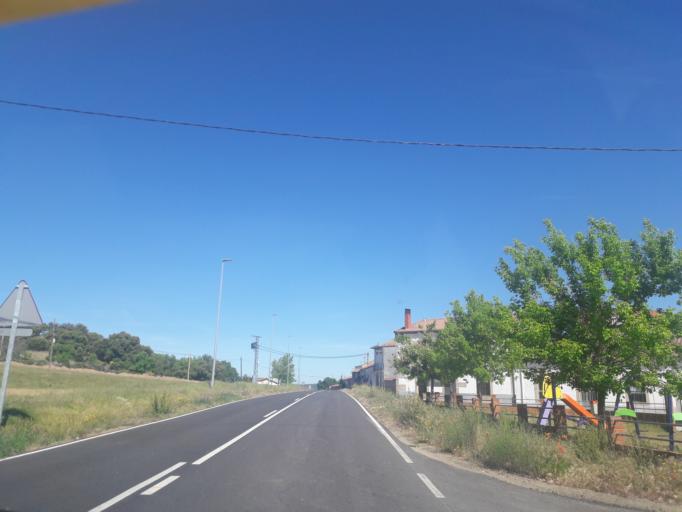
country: ES
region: Castille and Leon
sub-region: Provincia de Salamanca
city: Nava de Bejar
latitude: 40.4945
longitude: -5.6634
